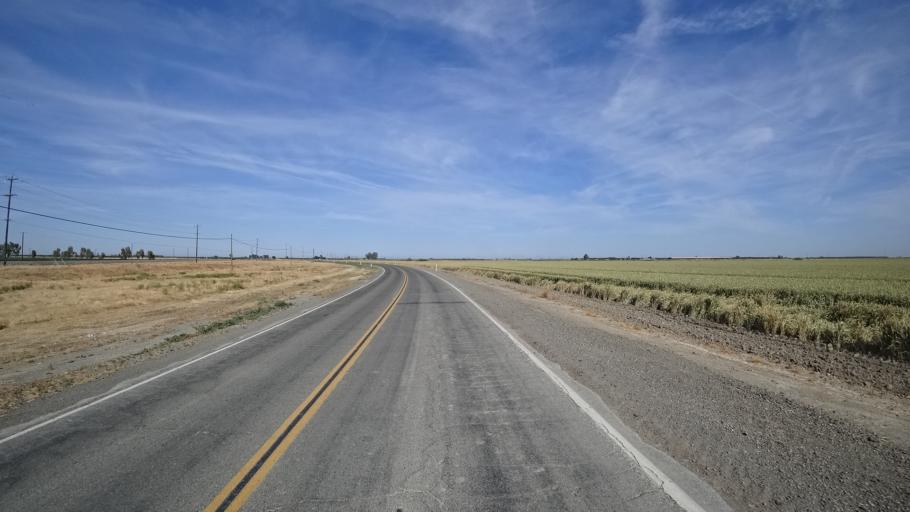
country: US
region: California
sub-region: Tulare County
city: Goshen
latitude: 36.3430
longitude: -119.5311
